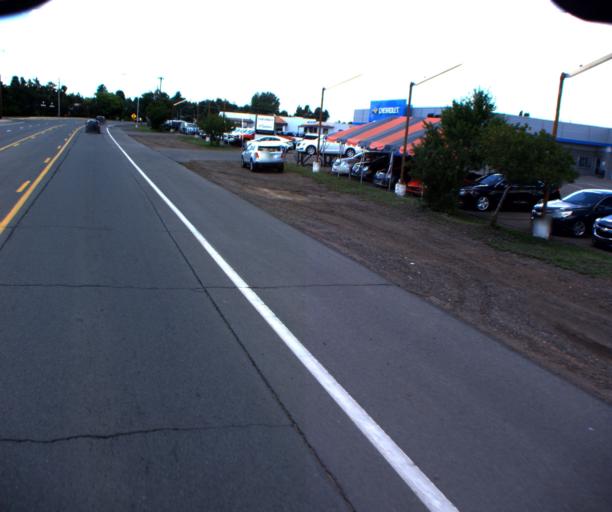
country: US
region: Arizona
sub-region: Coconino County
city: Flagstaff
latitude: 35.1898
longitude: -111.6655
